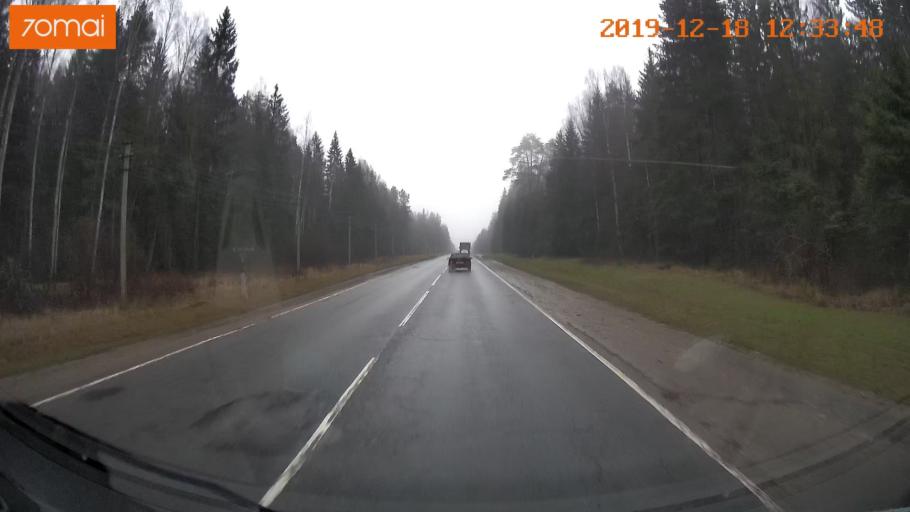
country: RU
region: Moskovskaya
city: Rumyantsevo
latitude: 56.1159
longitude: 36.5650
